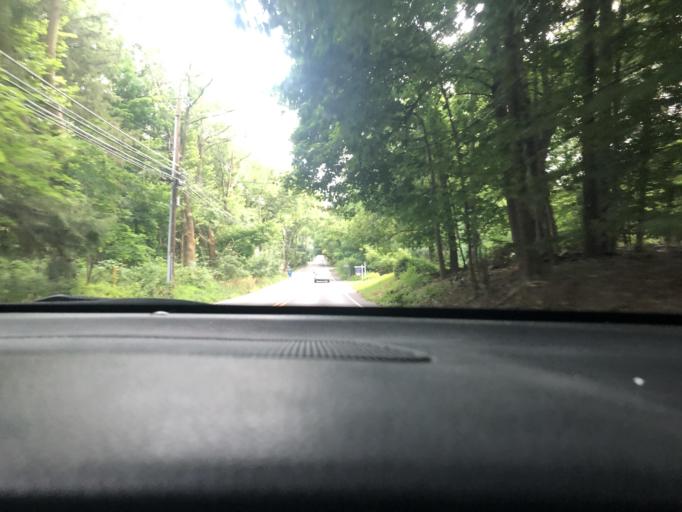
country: US
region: Pennsylvania
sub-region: Montgomery County
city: Spring House
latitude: 40.1762
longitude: -75.2368
